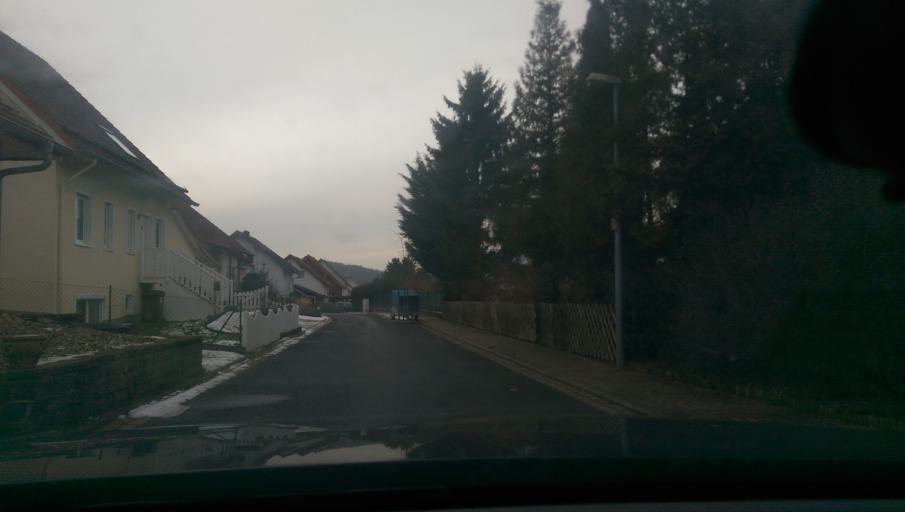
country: DE
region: Hesse
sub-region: Regierungsbezirk Kassel
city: Nieste
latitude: 51.3090
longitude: 9.6699
